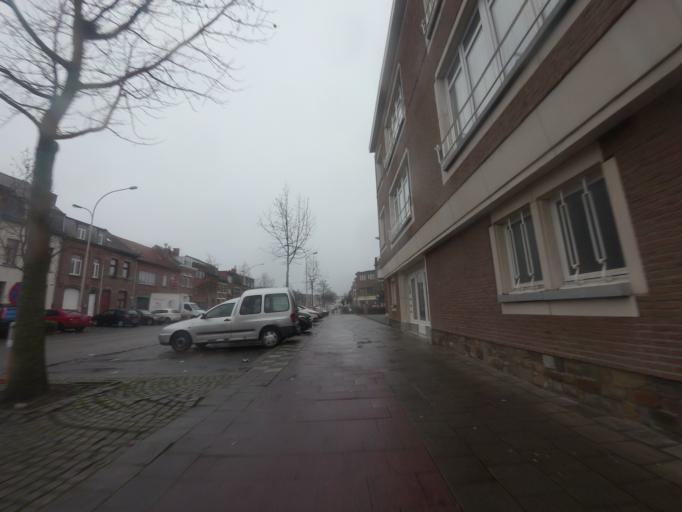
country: BE
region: Flanders
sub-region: Provincie Antwerpen
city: Hoboken
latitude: 51.1795
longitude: 4.3561
